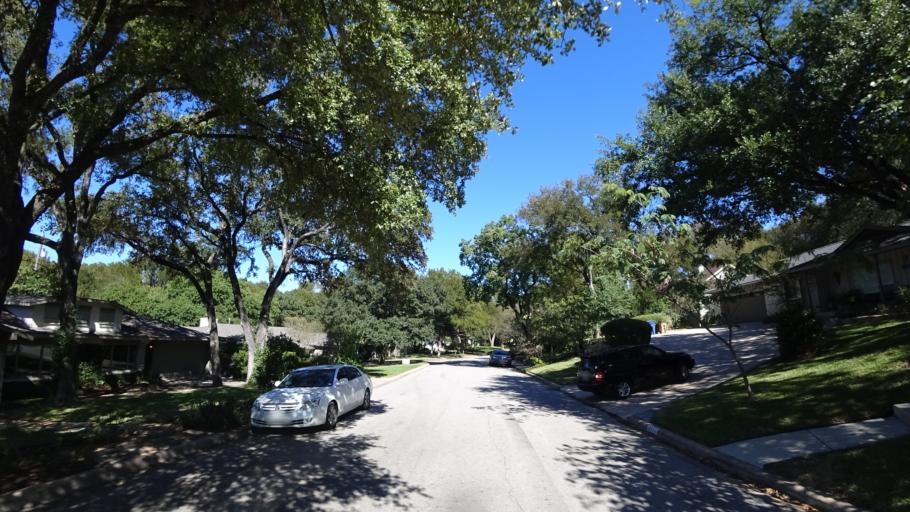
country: US
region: Texas
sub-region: Travis County
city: West Lake Hills
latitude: 30.3076
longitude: -97.7655
